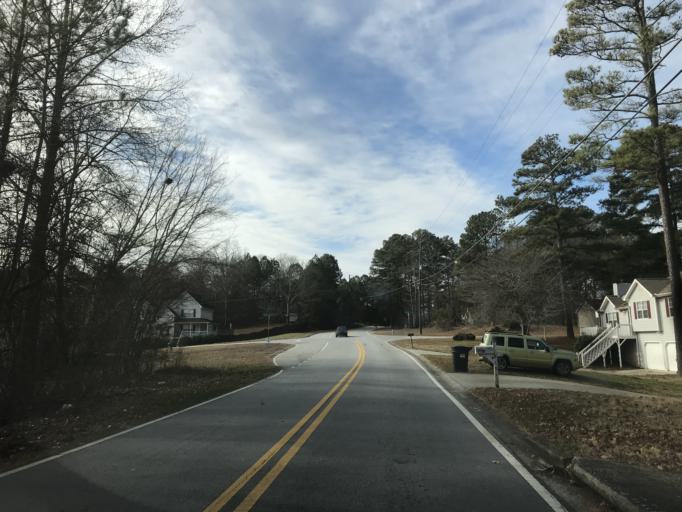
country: US
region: Georgia
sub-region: Douglas County
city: Douglasville
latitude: 33.7961
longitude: -84.8261
